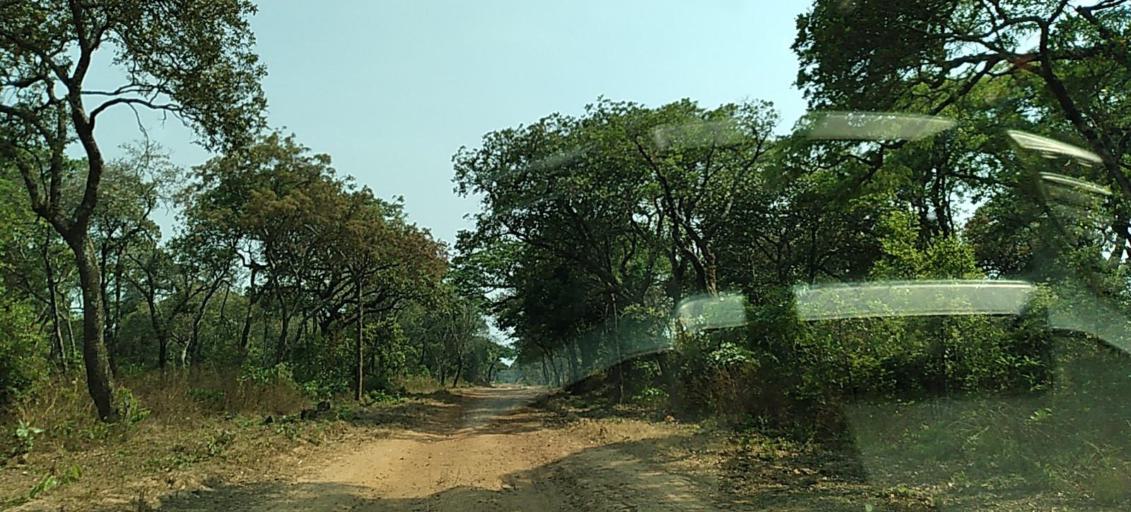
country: ZM
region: North-Western
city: Kansanshi
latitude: -12.0733
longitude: 26.8879
